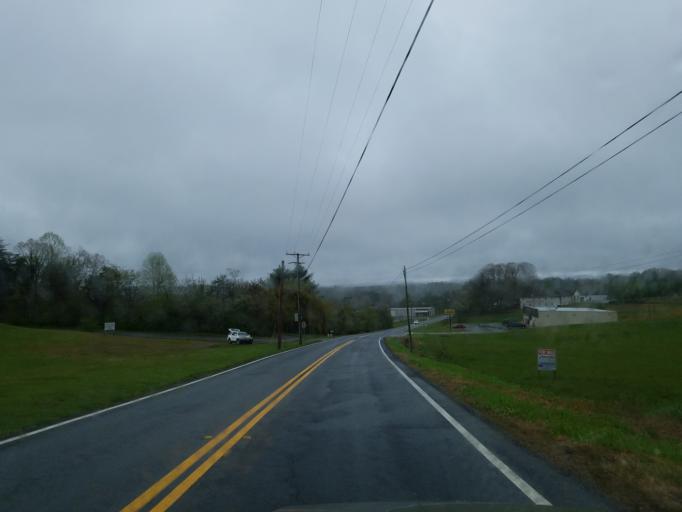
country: US
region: Georgia
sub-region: Fannin County
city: Blue Ridge
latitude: 34.8804
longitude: -84.2478
